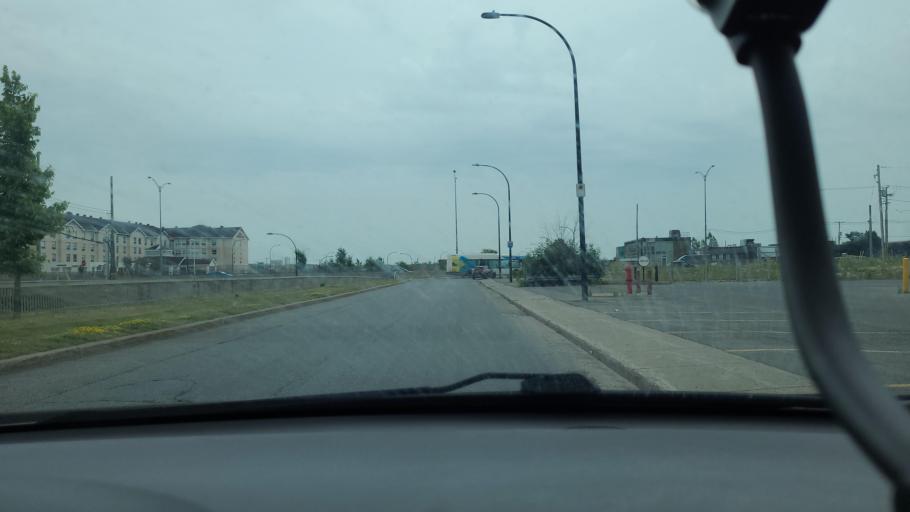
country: CA
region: Quebec
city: Cote-Saint-Luc
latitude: 45.4777
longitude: -73.7043
